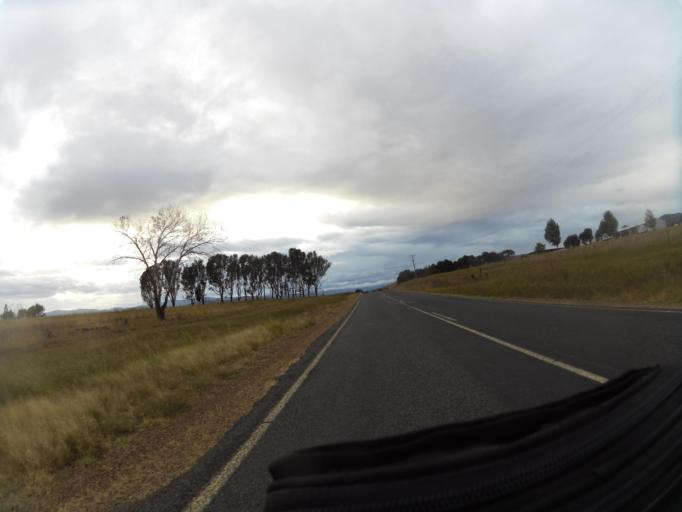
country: AU
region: New South Wales
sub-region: Greater Hume Shire
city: Holbrook
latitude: -36.0584
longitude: 147.9429
